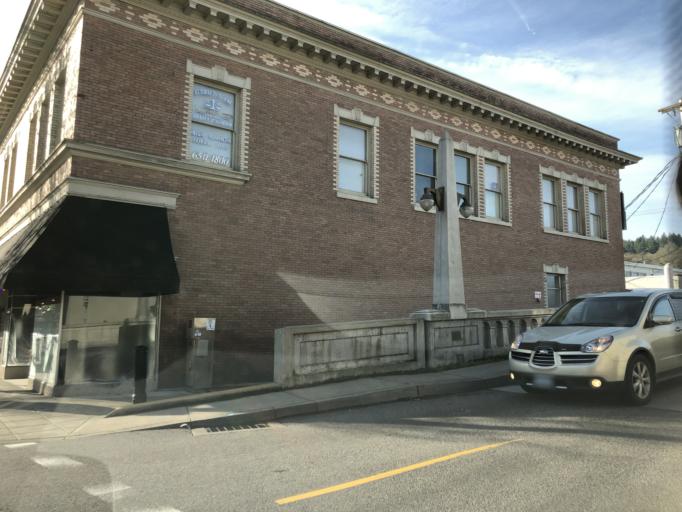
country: US
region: Oregon
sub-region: Clackamas County
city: Oregon City
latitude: 45.3578
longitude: -122.6086
